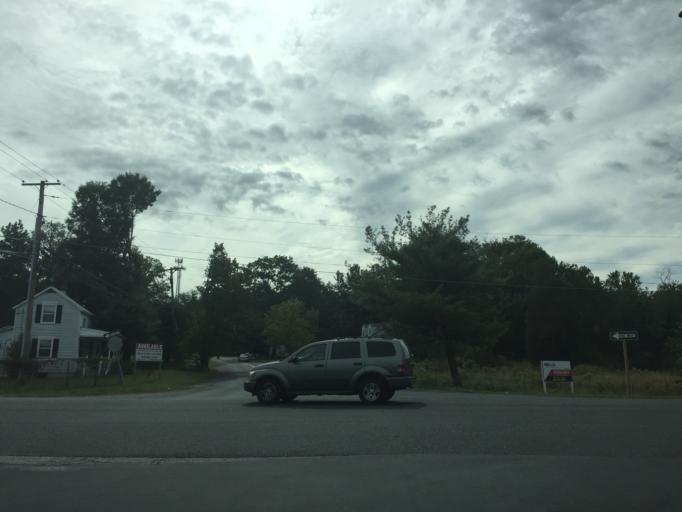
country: US
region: Maryland
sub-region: Harford County
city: Joppatowne
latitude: 39.4412
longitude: -76.3501
